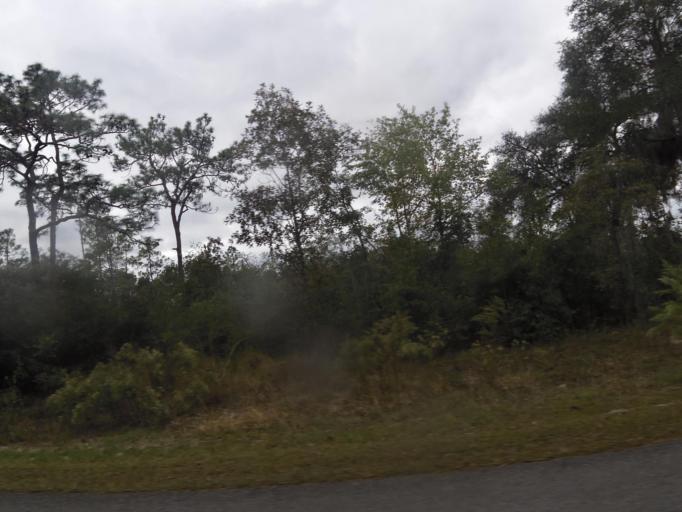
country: US
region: Florida
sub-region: Clay County
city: Keystone Heights
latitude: 29.8378
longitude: -81.9545
